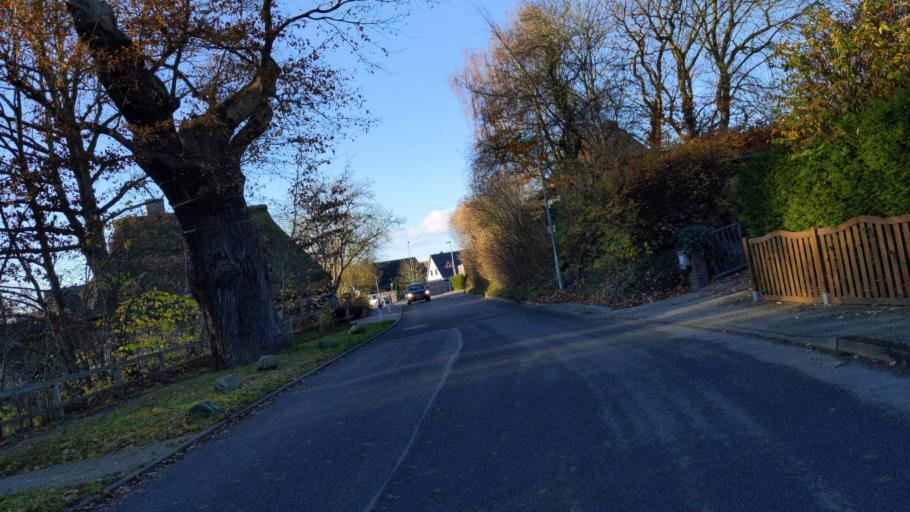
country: DE
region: Schleswig-Holstein
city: Ratekau
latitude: 53.9006
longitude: 10.7450
